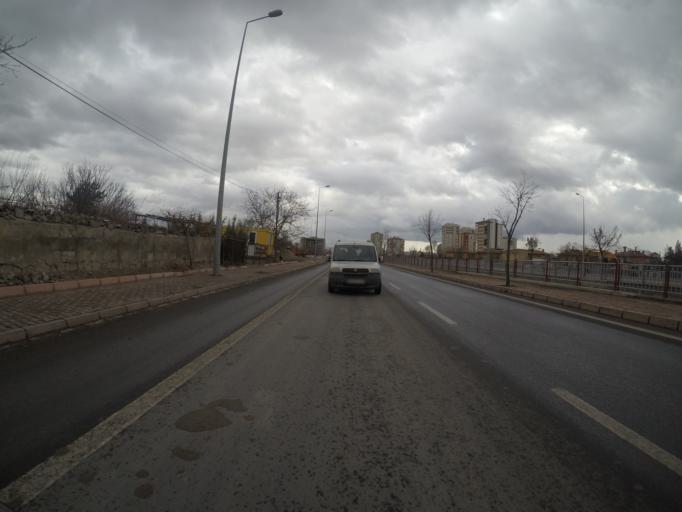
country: TR
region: Kayseri
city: Kayseri
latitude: 38.7501
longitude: 35.4725
